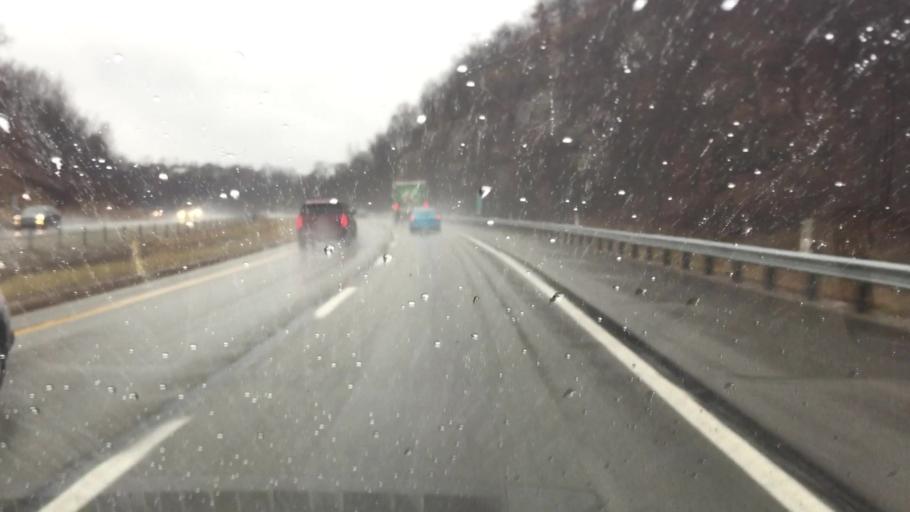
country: US
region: Pennsylvania
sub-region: Allegheny County
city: Franklin Park
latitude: 40.5582
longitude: -80.0844
